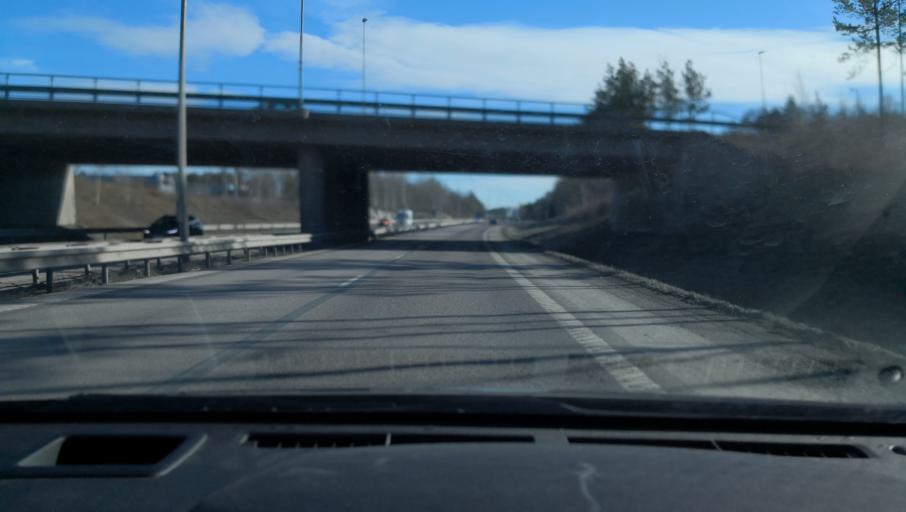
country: SE
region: Vaestmanland
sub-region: Vasteras
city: Vasteras
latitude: 59.6088
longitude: 16.5991
